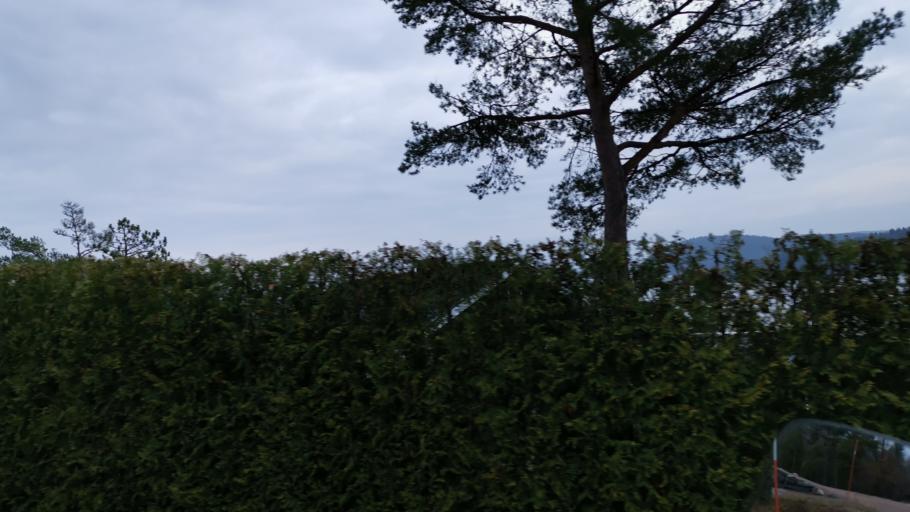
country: SE
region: Vaestra Goetaland
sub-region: Orust
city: Henan
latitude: 58.3395
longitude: 11.7214
